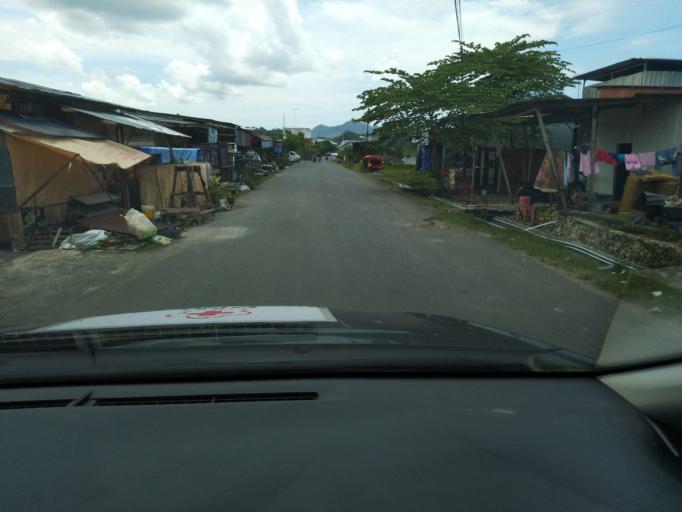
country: ID
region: Sulawesi Barat
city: Mamuju
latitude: -2.6813
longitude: 118.8808
